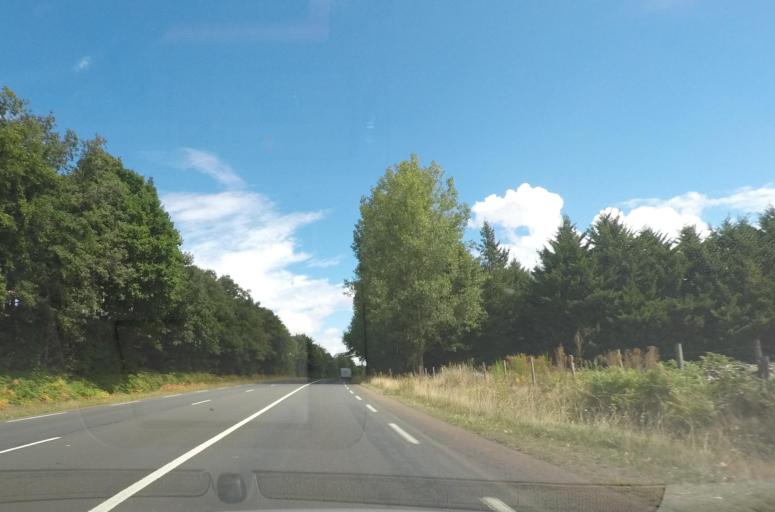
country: FR
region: Pays de la Loire
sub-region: Departement de la Sarthe
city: Parigne-le-Polin
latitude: 47.8497
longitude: 0.0935
